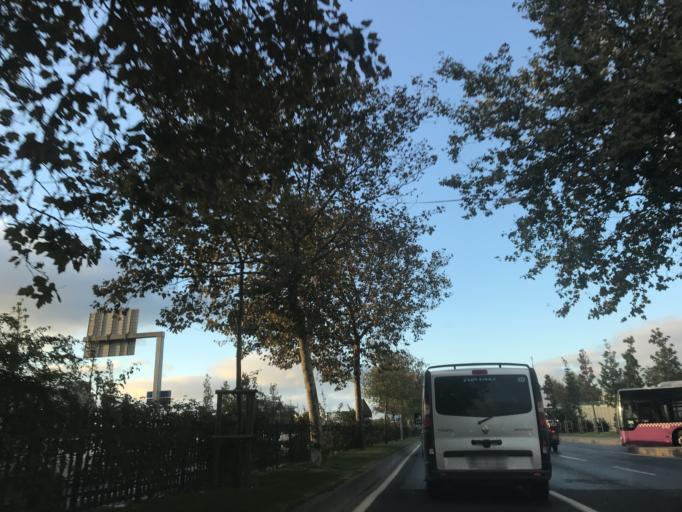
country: TR
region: Istanbul
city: Sisli
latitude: 41.1149
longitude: 29.0247
